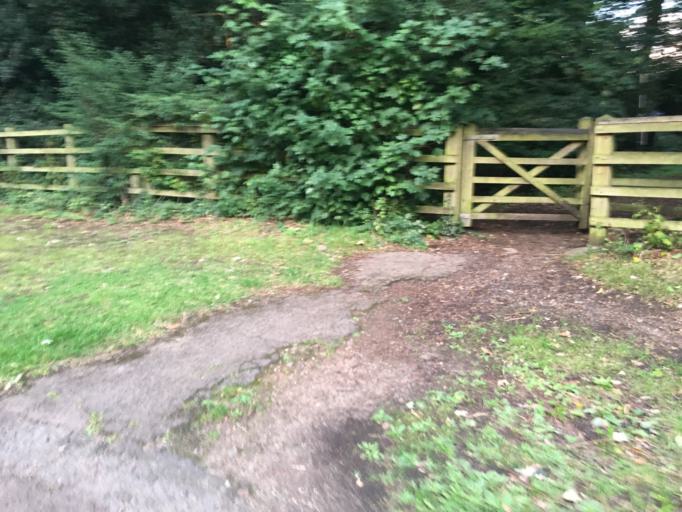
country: GB
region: England
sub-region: Coventry
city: Coventry
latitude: 52.3839
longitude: -1.5373
